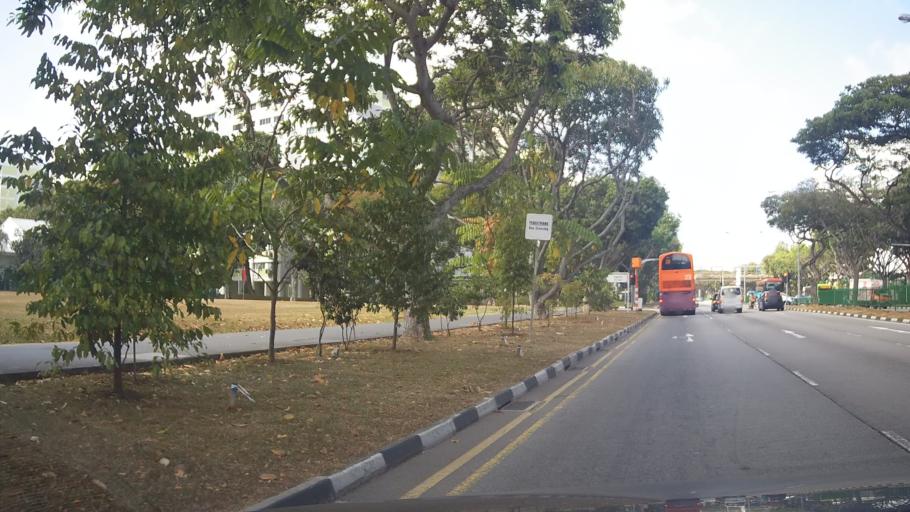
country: SG
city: Singapore
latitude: 1.3499
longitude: 103.9517
